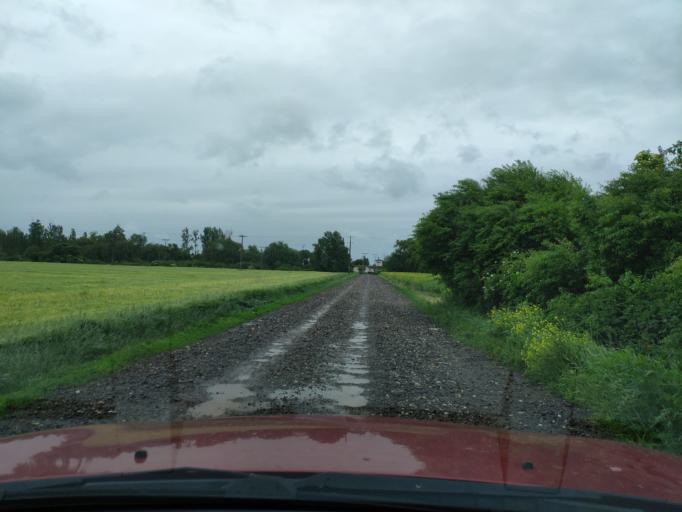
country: SK
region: Kosicky
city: Cierna nad Tisou
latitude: 48.4265
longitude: 22.0815
